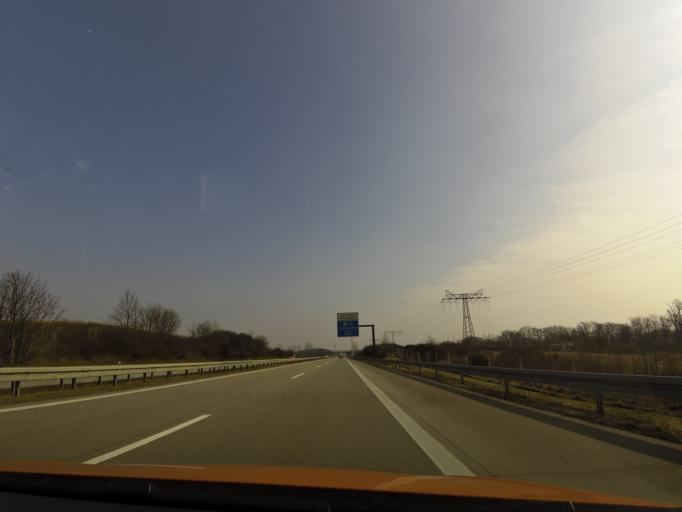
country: DE
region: Brandenburg
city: Frankfurt (Oder)
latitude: 52.3201
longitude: 14.4930
